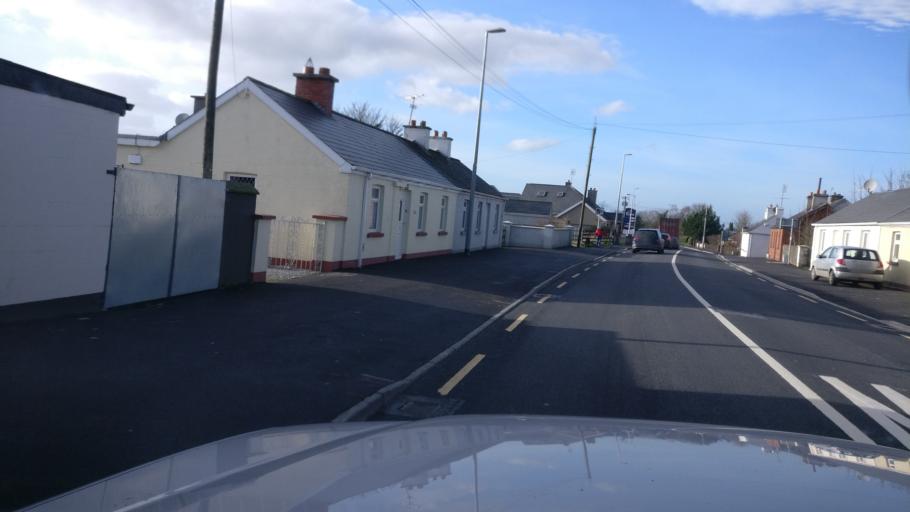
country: IE
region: Leinster
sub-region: Laois
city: Mountmellick
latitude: 53.1230
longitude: -7.3308
